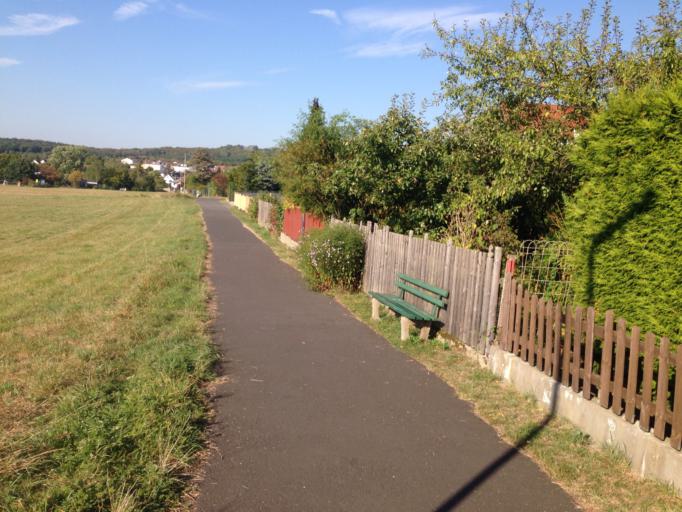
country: DE
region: Hesse
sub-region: Regierungsbezirk Giessen
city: Giessen
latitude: 50.5396
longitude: 8.7193
